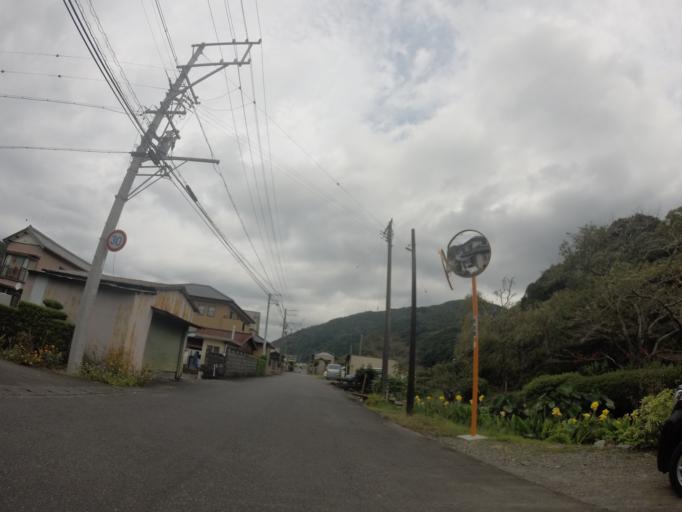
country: JP
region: Shizuoka
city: Fujieda
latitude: 34.9103
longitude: 138.1993
